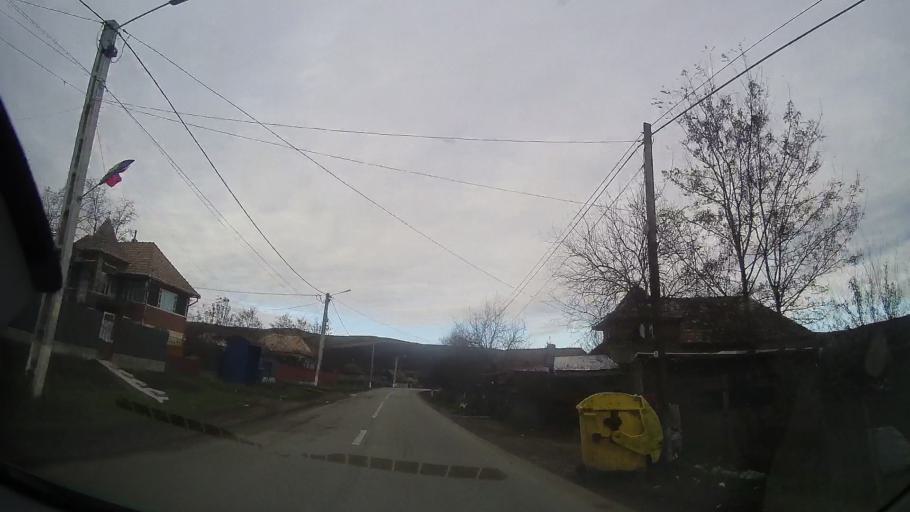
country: RO
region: Cluj
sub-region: Comuna Camarasu
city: Camarasu
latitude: 46.8177
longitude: 24.1373
